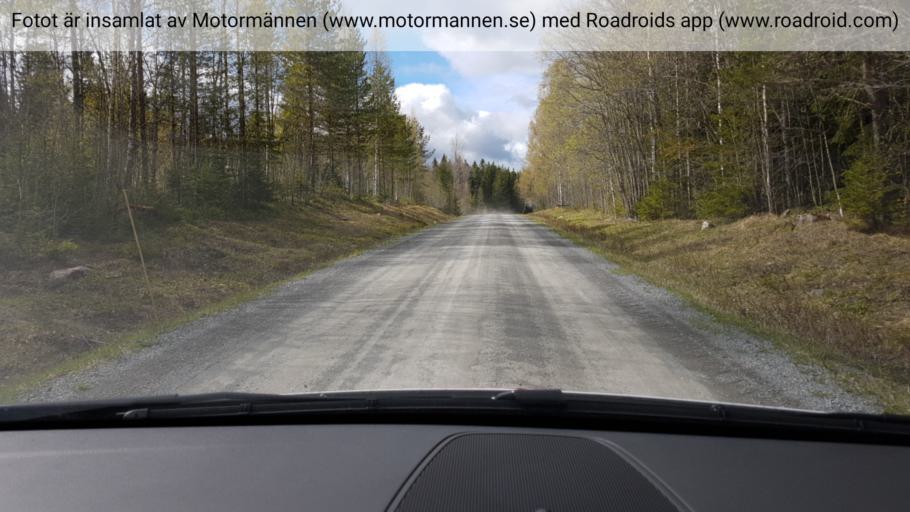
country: SE
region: Jaemtland
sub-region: OEstersunds Kommun
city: Brunflo
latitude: 63.1272
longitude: 15.0833
